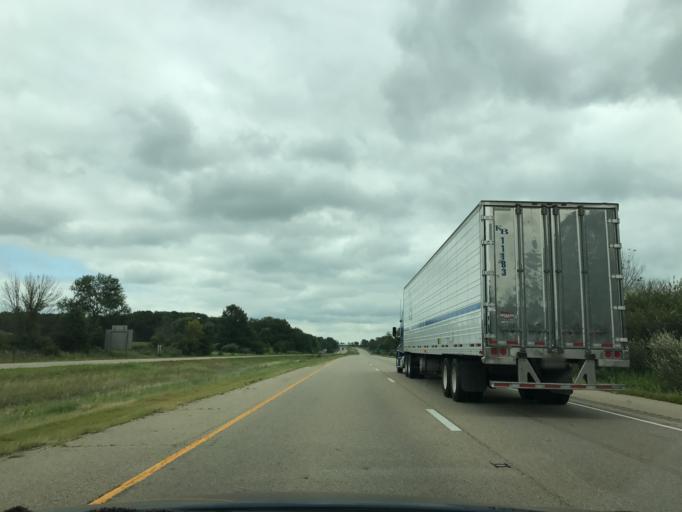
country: US
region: Illinois
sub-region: Bureau County
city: Depue
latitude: 41.4001
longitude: -89.3690
